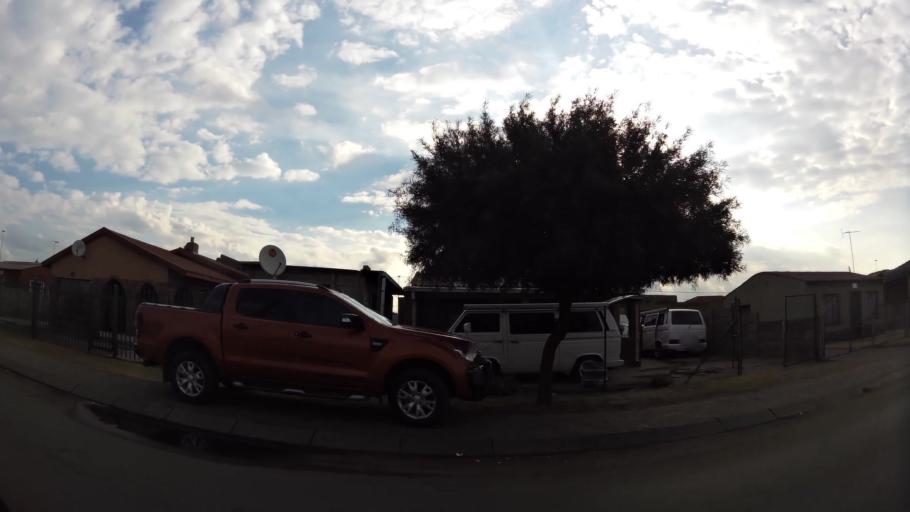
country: ZA
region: Gauteng
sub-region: Sedibeng District Municipality
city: Vanderbijlpark
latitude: -26.6922
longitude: 27.8752
